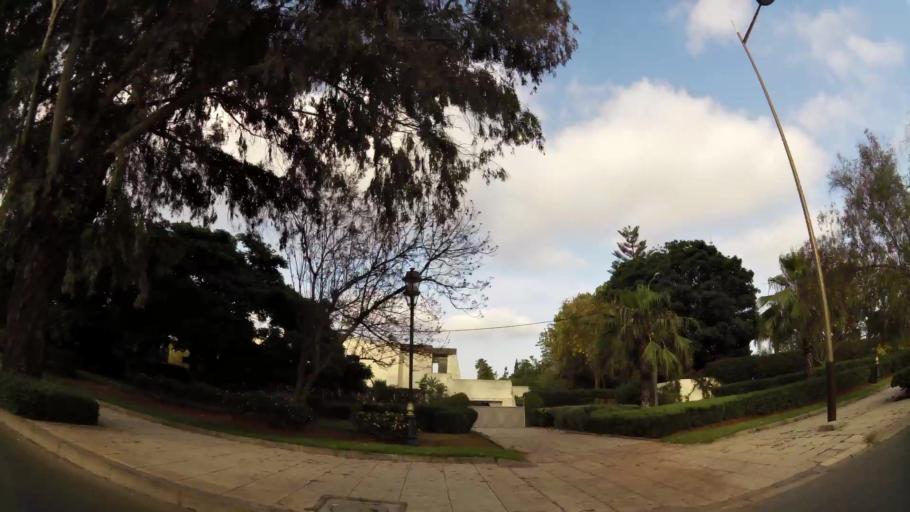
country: MA
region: Rabat-Sale-Zemmour-Zaer
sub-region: Rabat
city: Rabat
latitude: 33.9543
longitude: -6.8247
